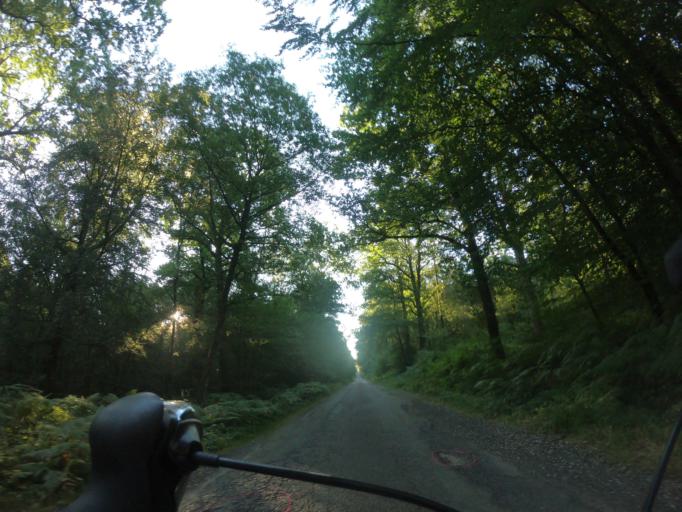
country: FR
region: Lower Normandy
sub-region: Departement de l'Orne
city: Magny-le-Desert
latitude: 48.5389
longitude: -0.3286
